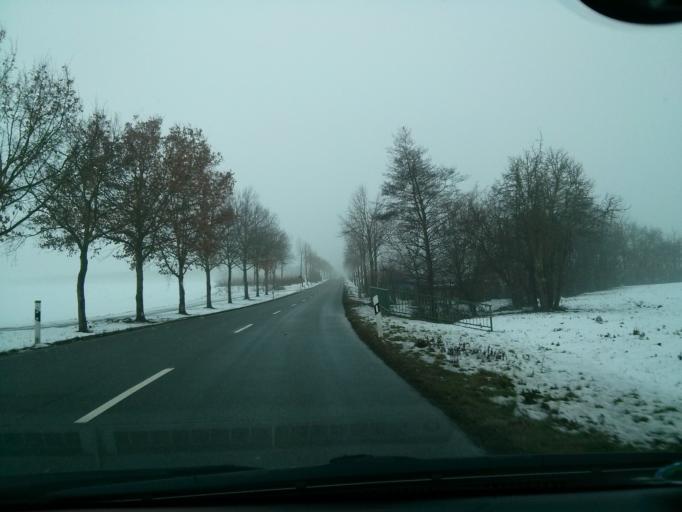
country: DE
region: North Rhine-Westphalia
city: Meckenheim
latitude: 50.6115
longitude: 7.0204
